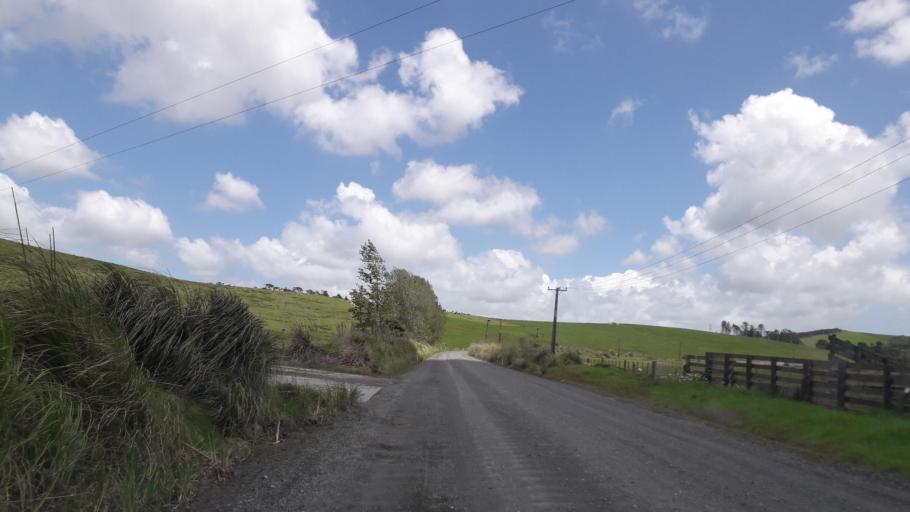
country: NZ
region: Northland
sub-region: Far North District
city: Taipa
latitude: -35.0111
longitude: 173.4257
